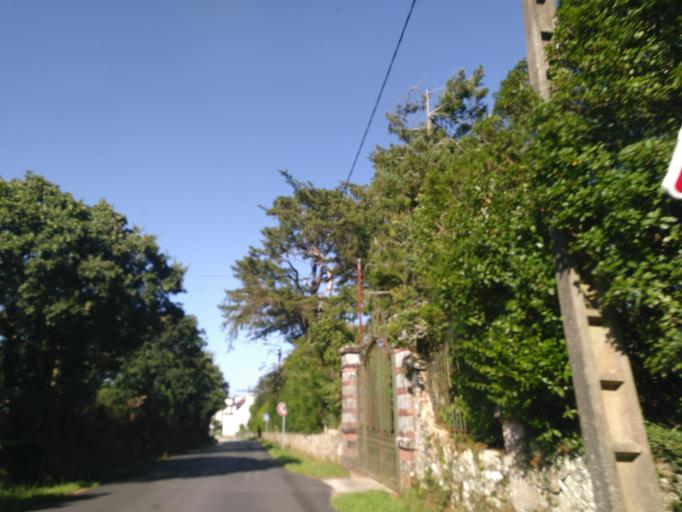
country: FR
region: Brittany
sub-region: Departement du Finistere
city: Le Faou
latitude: 48.2902
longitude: -4.1815
